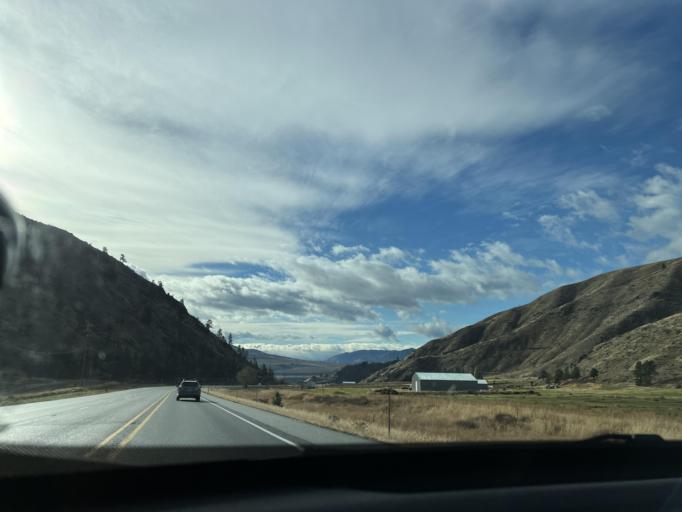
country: US
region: Washington
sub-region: Chelan County
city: Manson
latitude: 47.7915
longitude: -120.1342
